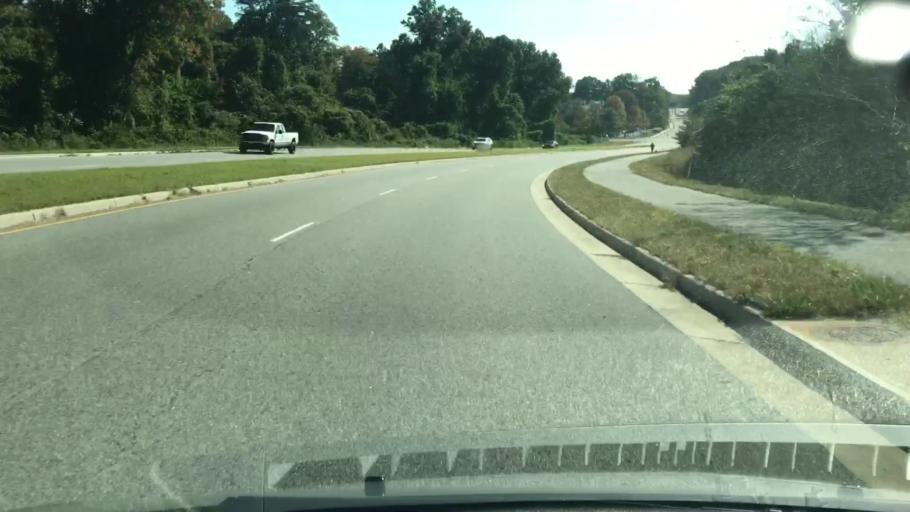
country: US
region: Virginia
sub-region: Fairfax County
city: Woodlawn
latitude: 38.7260
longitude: -77.1380
